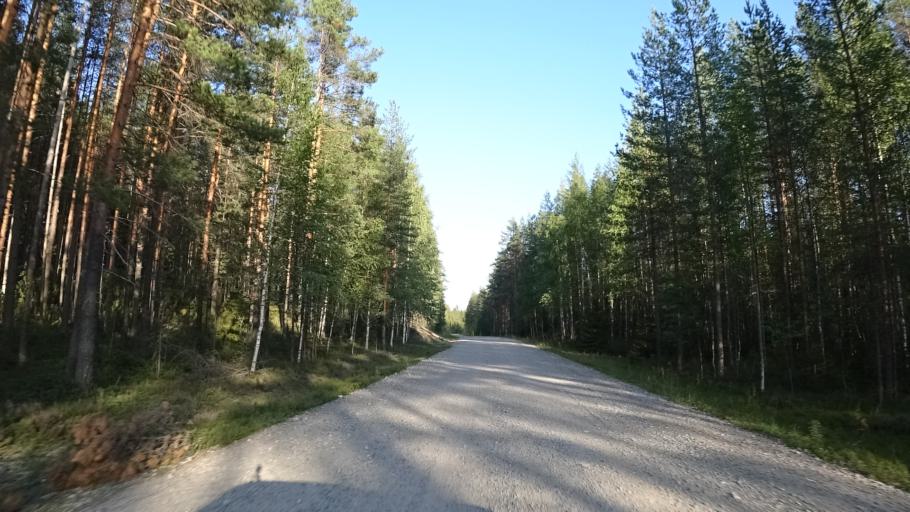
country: FI
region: North Karelia
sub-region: Joensuu
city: Ilomantsi
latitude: 63.1384
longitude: 30.6970
